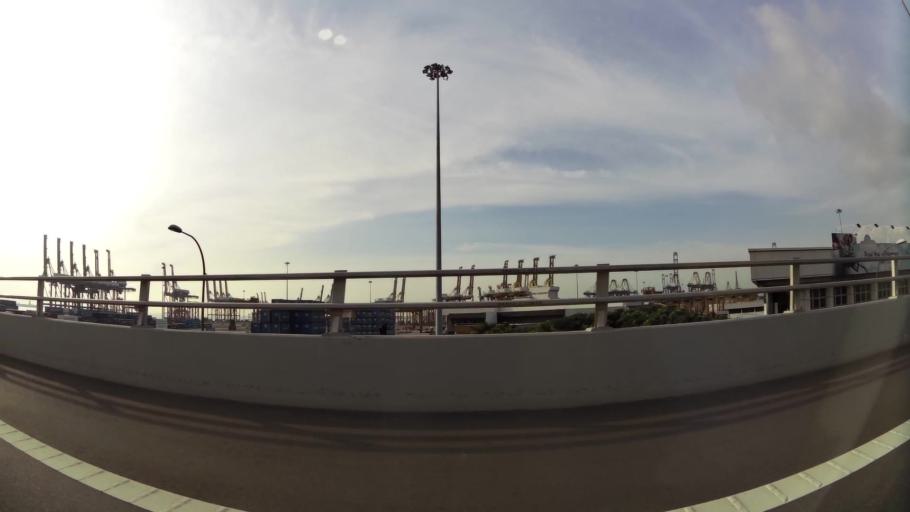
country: SG
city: Singapore
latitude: 1.2722
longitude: 103.8472
